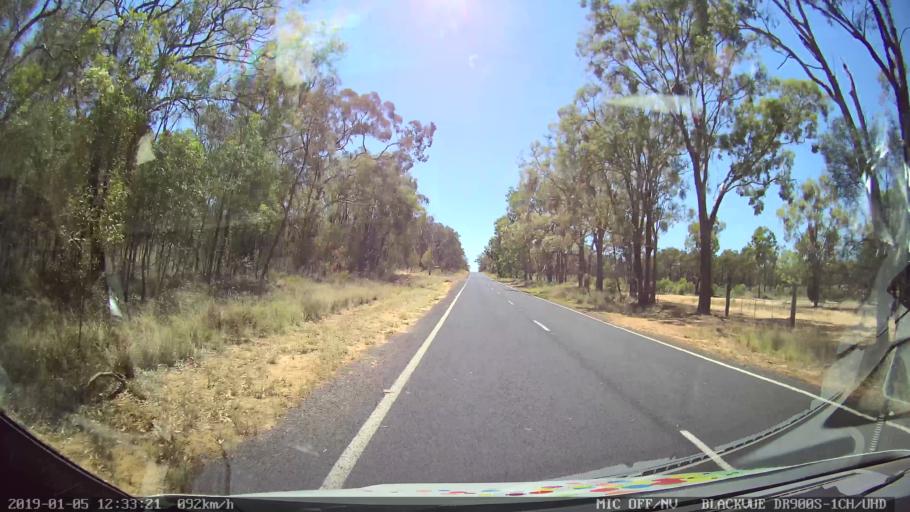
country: AU
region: New South Wales
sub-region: Warrumbungle Shire
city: Coonabarabran
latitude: -31.2149
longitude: 149.3937
